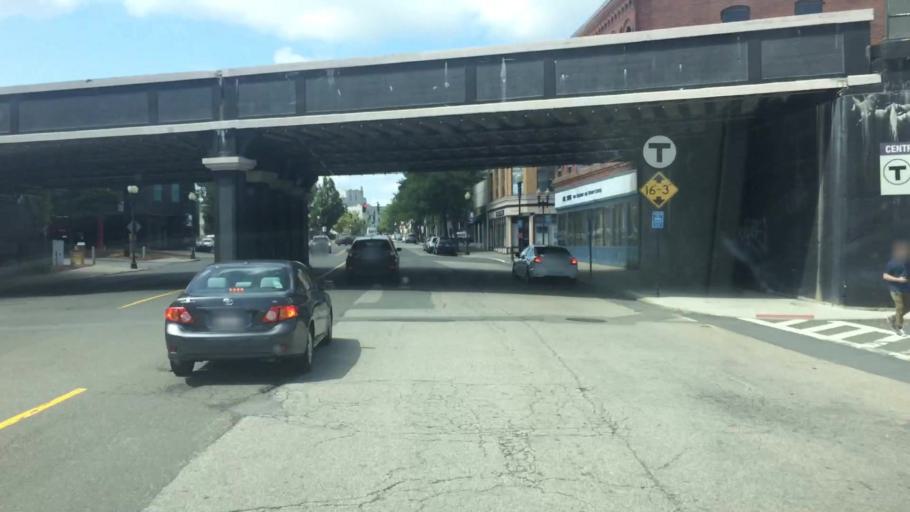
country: US
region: Massachusetts
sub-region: Essex County
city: Lynn
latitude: 42.4618
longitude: -70.9469
